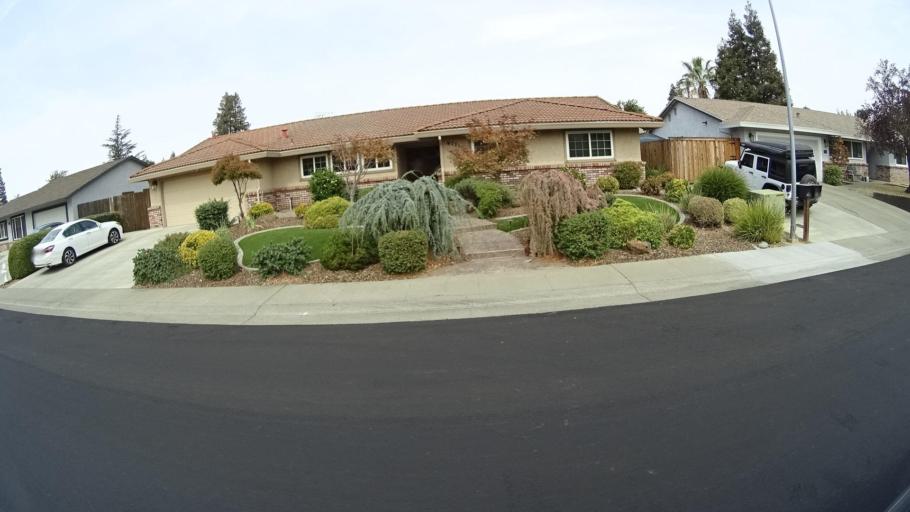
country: US
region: California
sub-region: Sacramento County
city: Elk Grove
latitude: 38.4113
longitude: -121.3822
